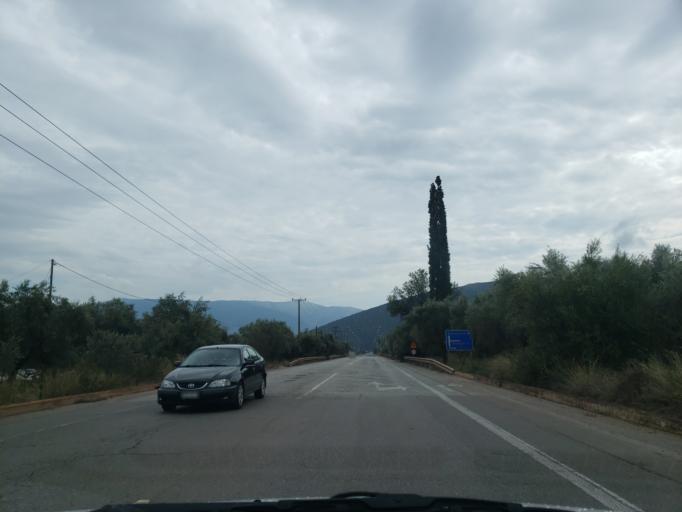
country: GR
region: Central Greece
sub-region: Nomos Fokidos
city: Amfissa
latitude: 38.4945
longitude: 22.4126
